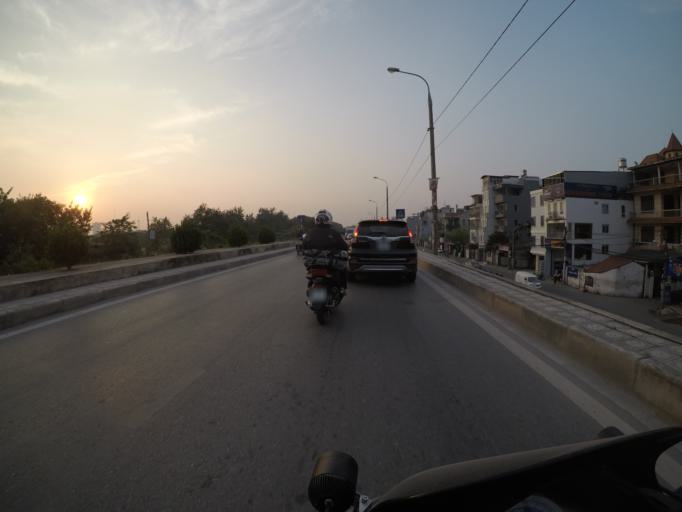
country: VN
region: Ha Noi
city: Hoan Kiem
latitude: 21.0342
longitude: 105.8747
